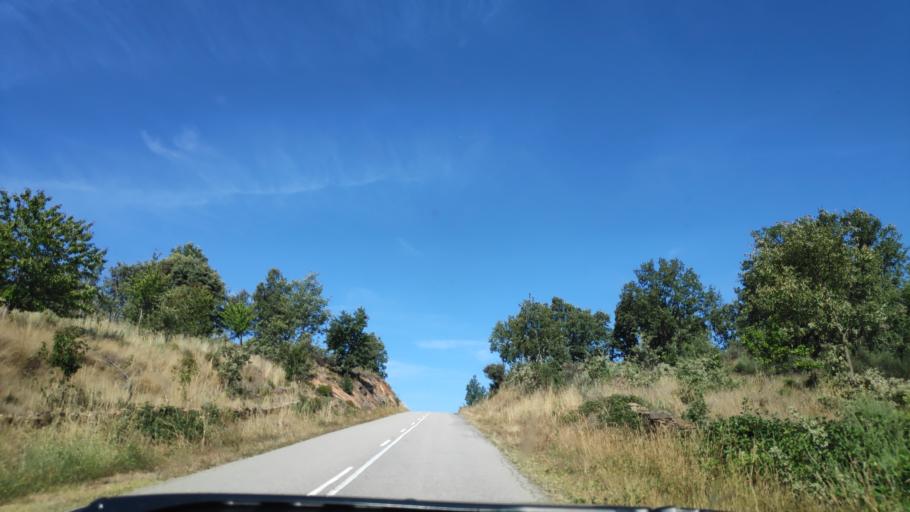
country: ES
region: Castille and Leon
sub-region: Provincia de Zamora
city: Alcanices
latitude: 41.6427
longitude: -6.3565
